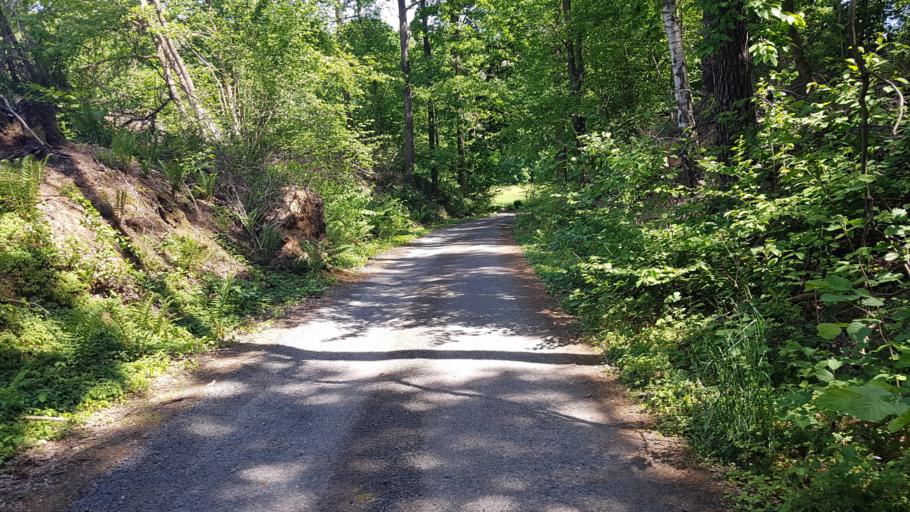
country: DE
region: Brandenburg
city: Grosskmehlen
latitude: 51.3642
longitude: 13.7079
